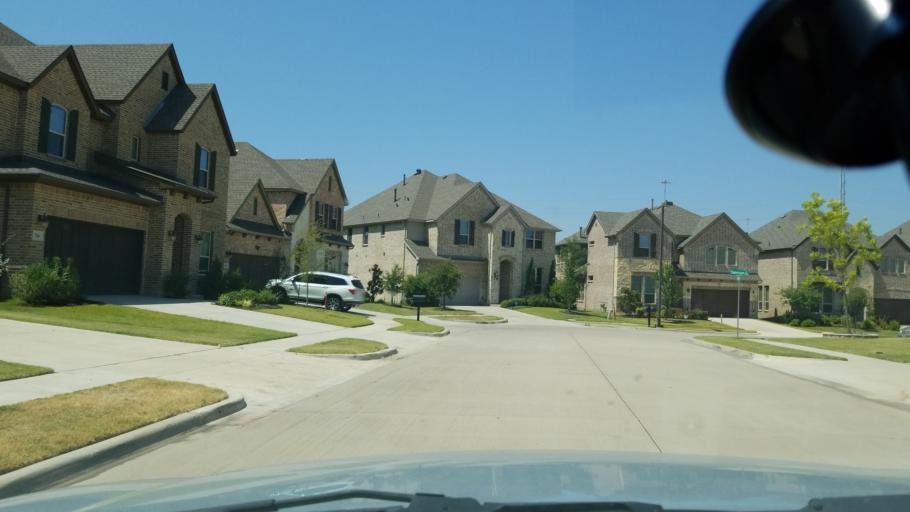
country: US
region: Texas
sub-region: Dallas County
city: Farmers Branch
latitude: 32.9143
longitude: -96.9419
